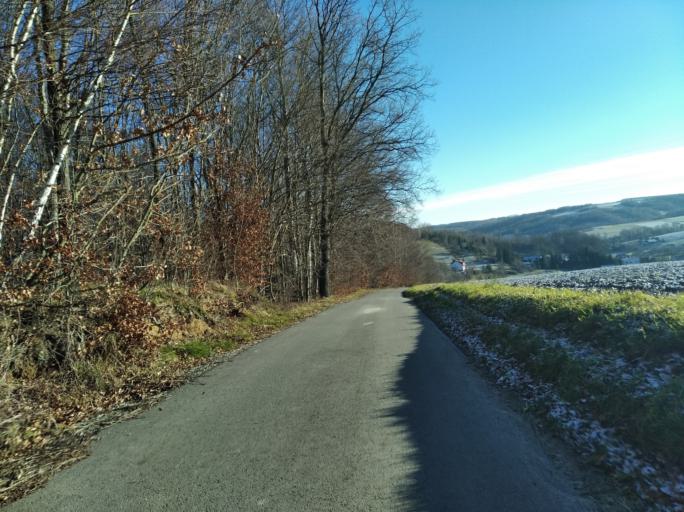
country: PL
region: Subcarpathian Voivodeship
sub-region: Powiat strzyzowski
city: Strzyzow
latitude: 49.9341
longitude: 21.7689
